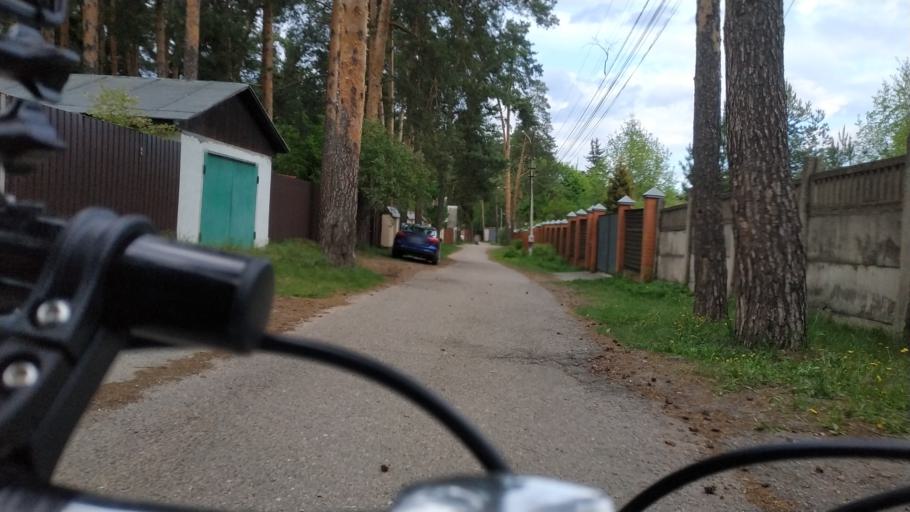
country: RU
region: Moskovskaya
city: Kratovo
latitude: 55.5923
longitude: 38.1517
